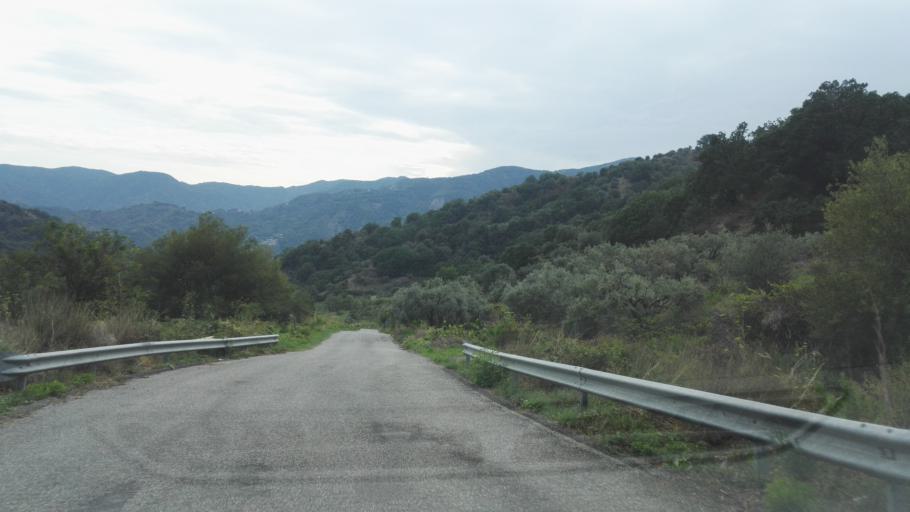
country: IT
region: Calabria
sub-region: Provincia di Reggio Calabria
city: Caulonia
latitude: 38.4347
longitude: 16.3981
